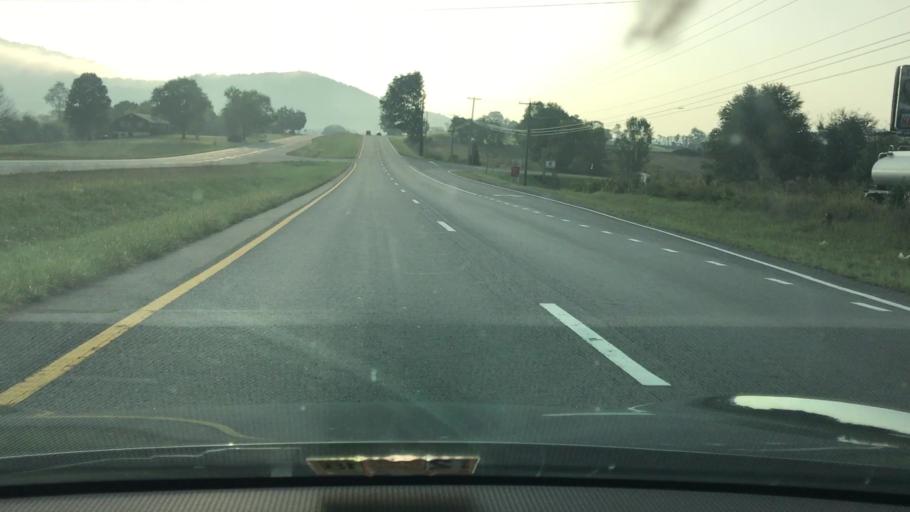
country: US
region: Virginia
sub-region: Botetourt County
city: Blue Ridge
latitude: 37.3783
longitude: -79.7147
